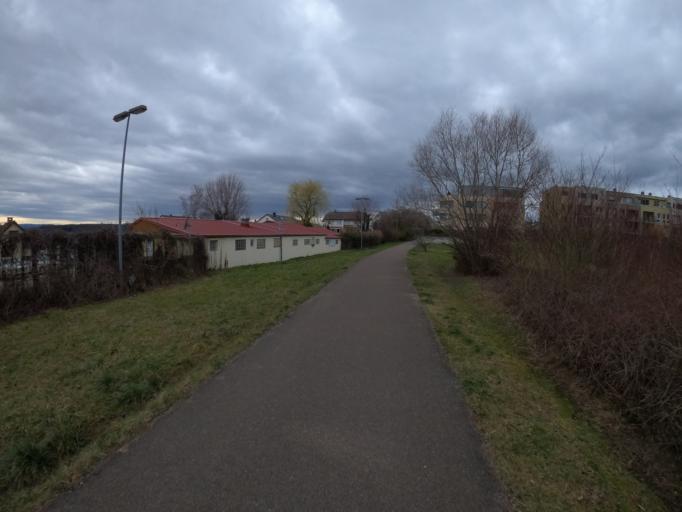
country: DE
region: Baden-Wuerttemberg
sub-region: Regierungsbezirk Stuttgart
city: Eislingen
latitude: 48.7035
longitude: 9.6861
